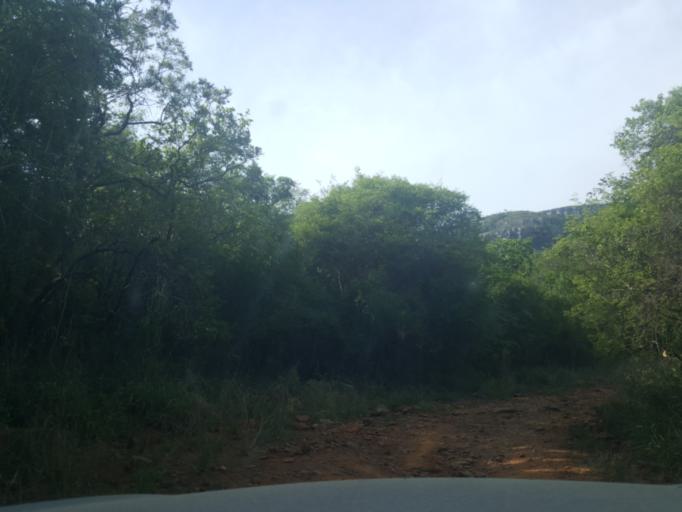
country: ZA
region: Limpopo
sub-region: Mopani District Municipality
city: Hoedspruit
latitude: -24.5911
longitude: 30.8284
